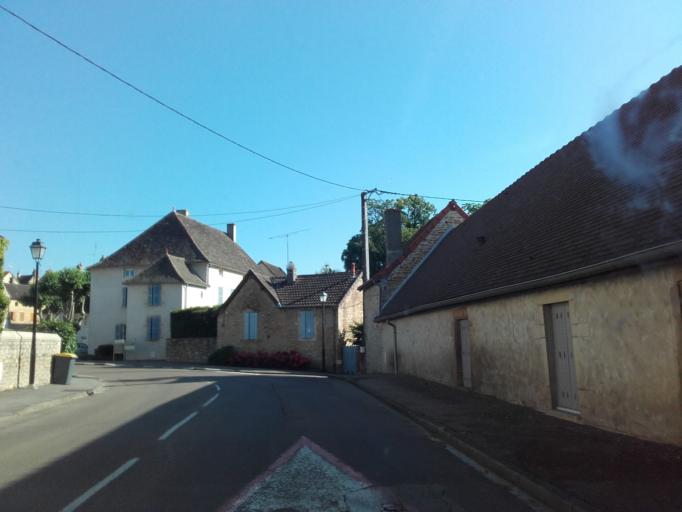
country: FR
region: Bourgogne
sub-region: Departement de Saone-et-Loire
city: Buxy
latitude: 46.7105
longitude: 4.6948
